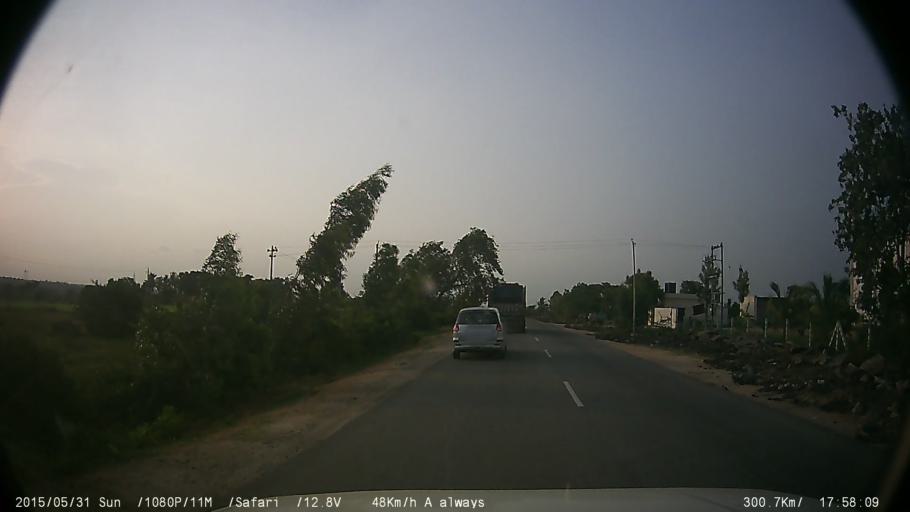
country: IN
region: Karnataka
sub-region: Mysore
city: Nanjangud
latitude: 12.0070
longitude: 76.6694
